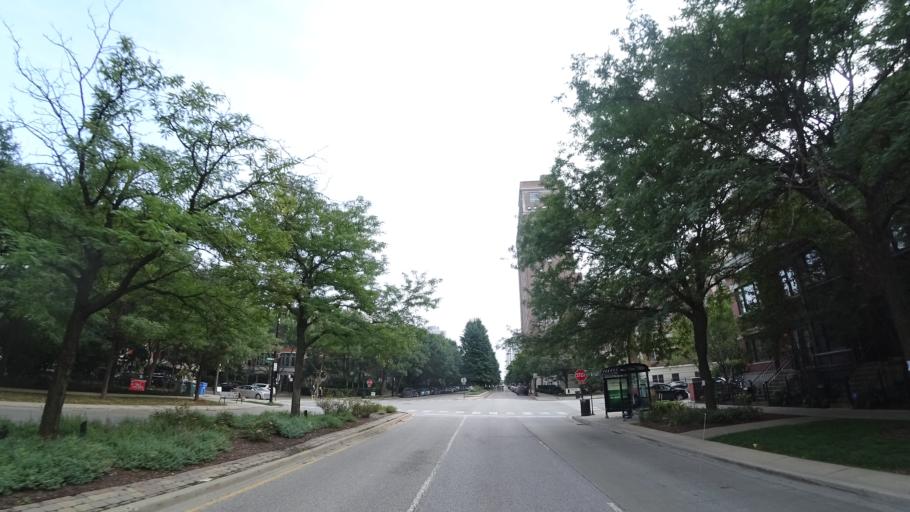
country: US
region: Illinois
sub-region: Cook County
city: Chicago
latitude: 41.8645
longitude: -87.6225
